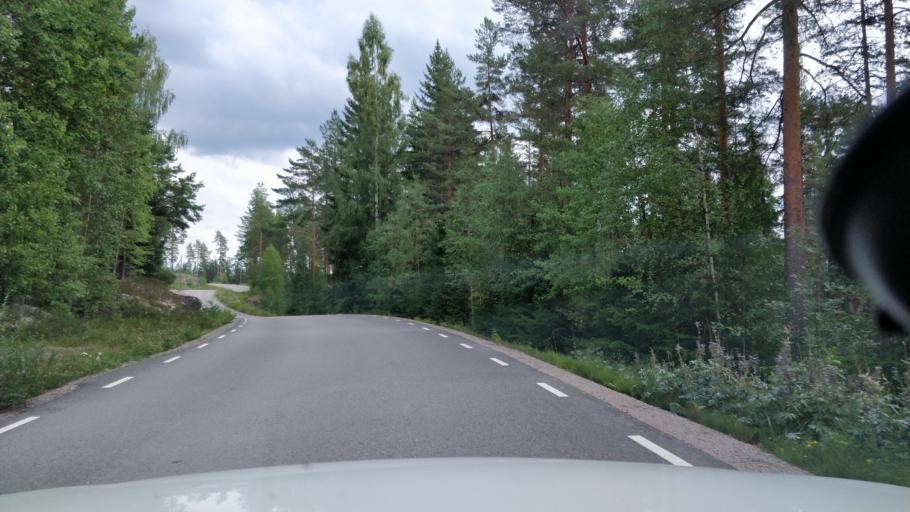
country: SE
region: Dalarna
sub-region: Faluns Kommun
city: Bjursas
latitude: 60.7423
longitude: 15.5371
